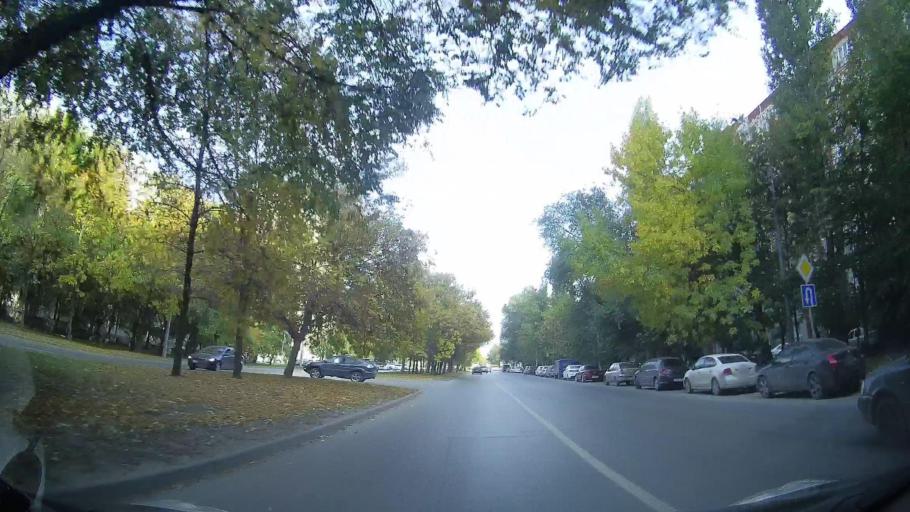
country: RU
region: Rostov
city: Imeni Chkalova
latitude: 47.2810
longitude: 39.7640
